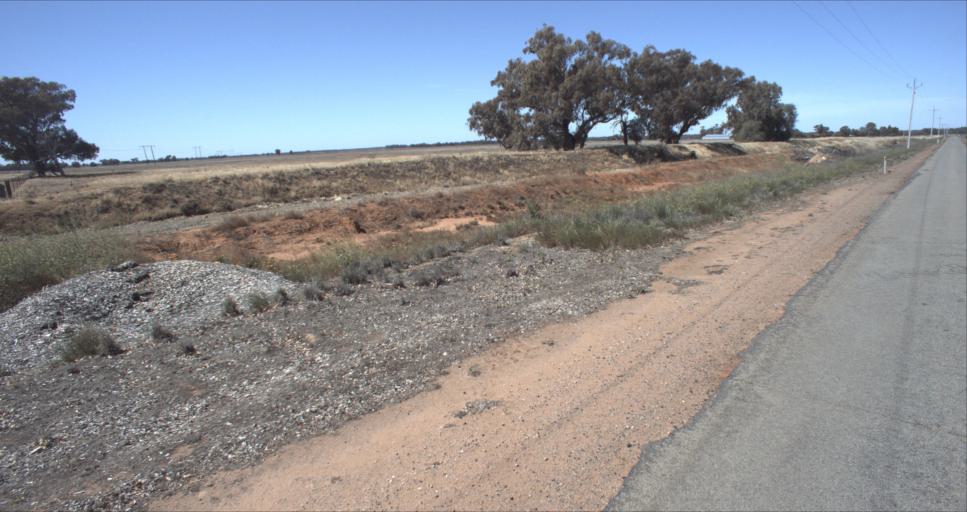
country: AU
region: New South Wales
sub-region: Leeton
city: Leeton
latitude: -34.5756
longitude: 146.3098
